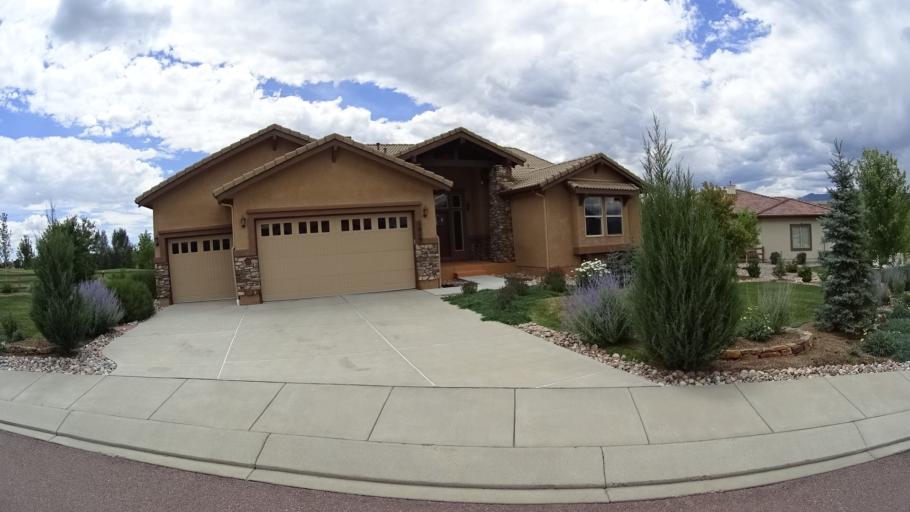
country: US
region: Colorado
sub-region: El Paso County
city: Gleneagle
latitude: 39.0230
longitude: -104.7991
